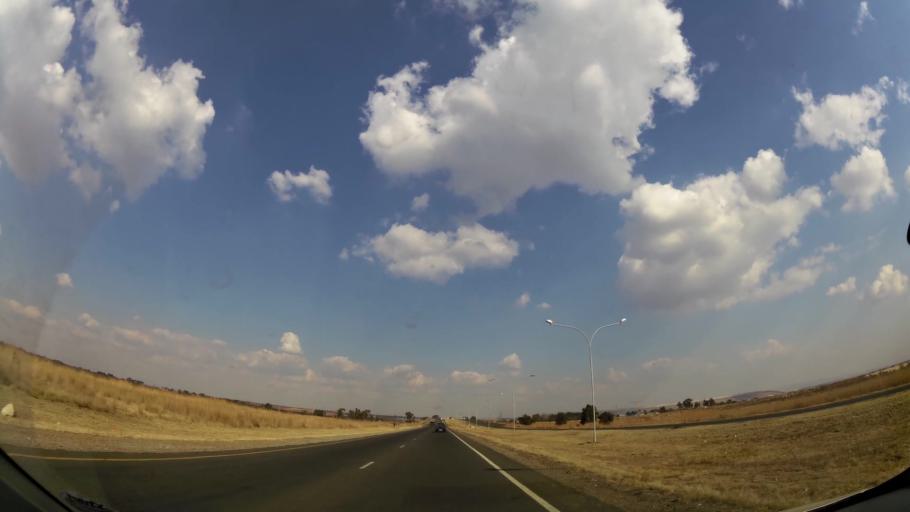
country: ZA
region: Gauteng
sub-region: Ekurhuleni Metropolitan Municipality
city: Brakpan
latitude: -26.2876
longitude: 28.3323
